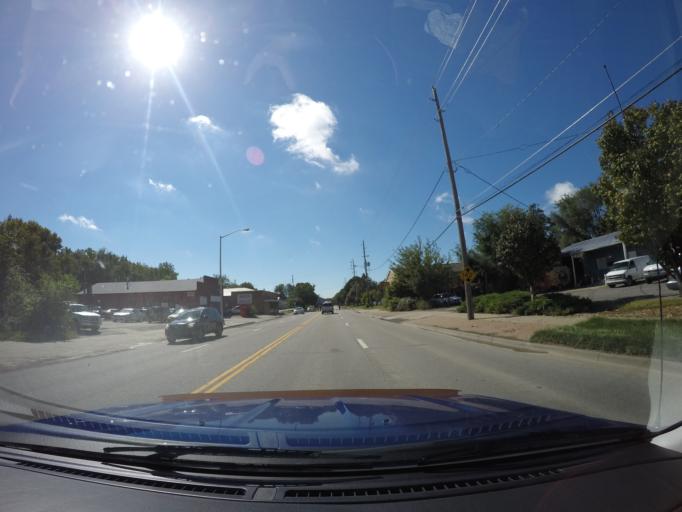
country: US
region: Kansas
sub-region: Douglas County
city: Lawrence
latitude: 38.9815
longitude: -95.2354
